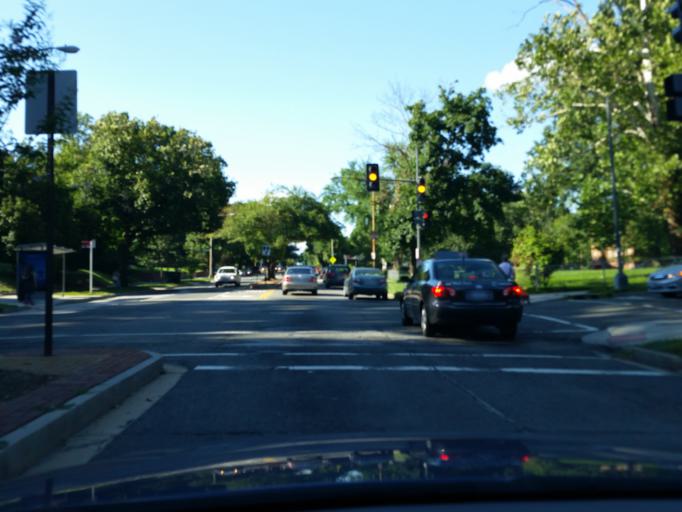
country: US
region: Maryland
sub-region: Montgomery County
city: Silver Spring
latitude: 38.9660
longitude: -77.0363
